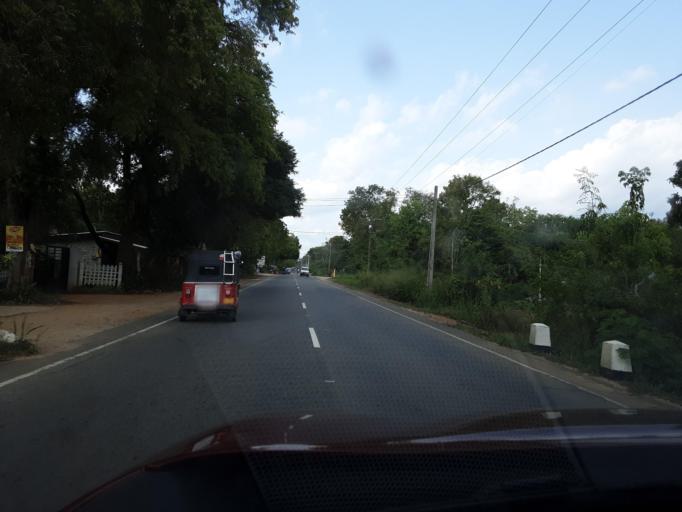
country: LK
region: Uva
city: Haputale
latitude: 6.5286
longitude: 81.1266
